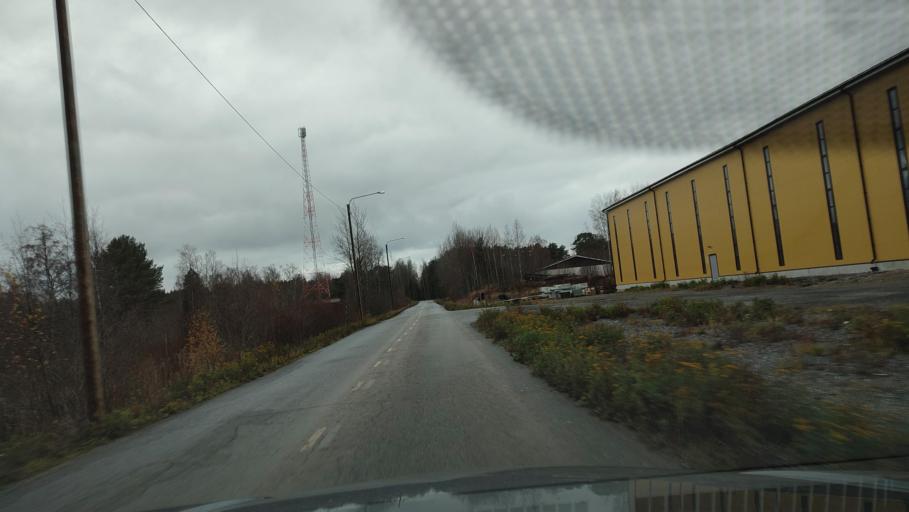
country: FI
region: Ostrobothnia
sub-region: Sydosterbotten
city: Kristinestad
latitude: 62.2782
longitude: 21.4049
